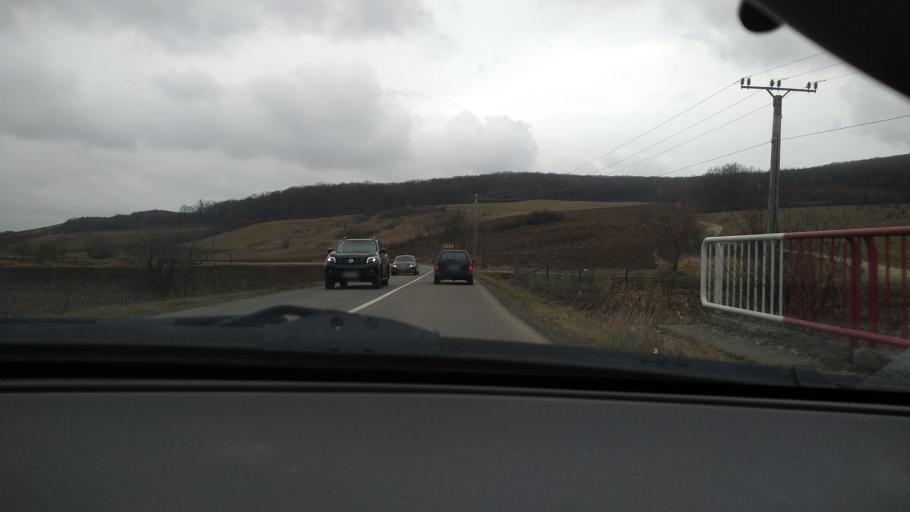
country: RO
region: Mures
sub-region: Comuna Bereni
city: Bereni
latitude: 46.5478
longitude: 24.8430
